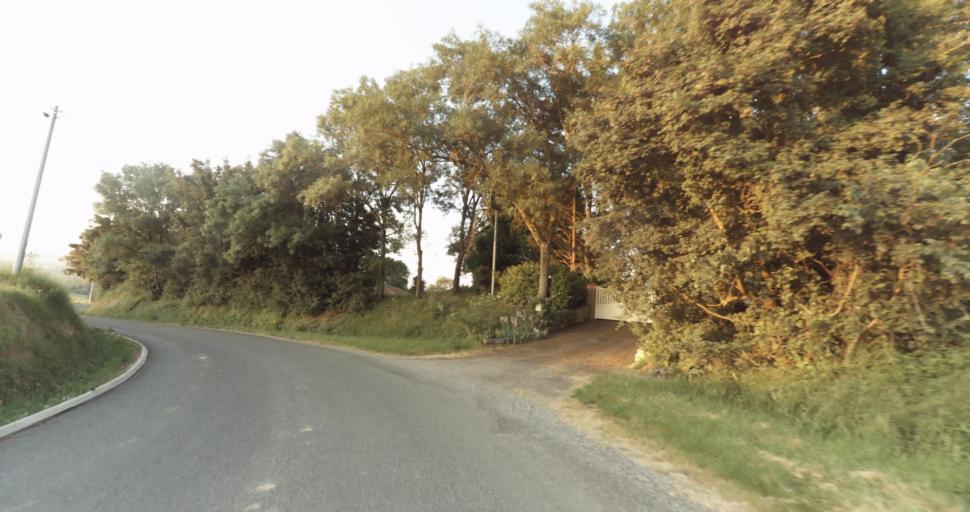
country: FR
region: Midi-Pyrenees
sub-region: Departement du Gers
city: Pujaudran
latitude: 43.6469
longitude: 1.1072
